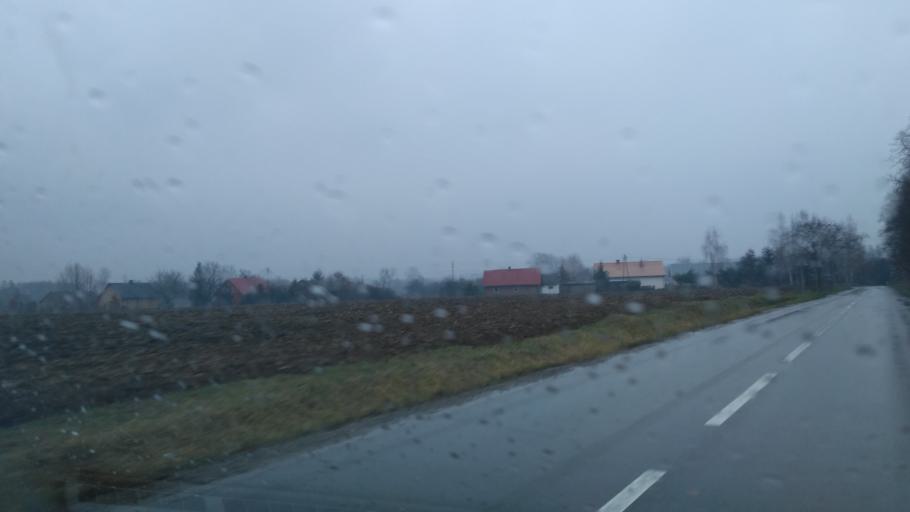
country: PL
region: Subcarpathian Voivodeship
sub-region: Powiat lancucki
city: Czarna
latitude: 50.0877
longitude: 22.1694
